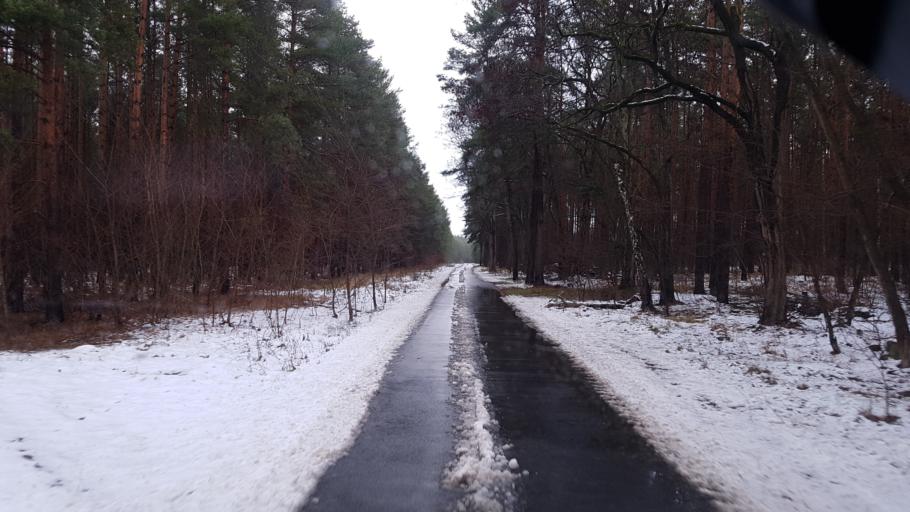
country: DE
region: Brandenburg
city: Straupitz
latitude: 51.9652
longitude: 14.1683
